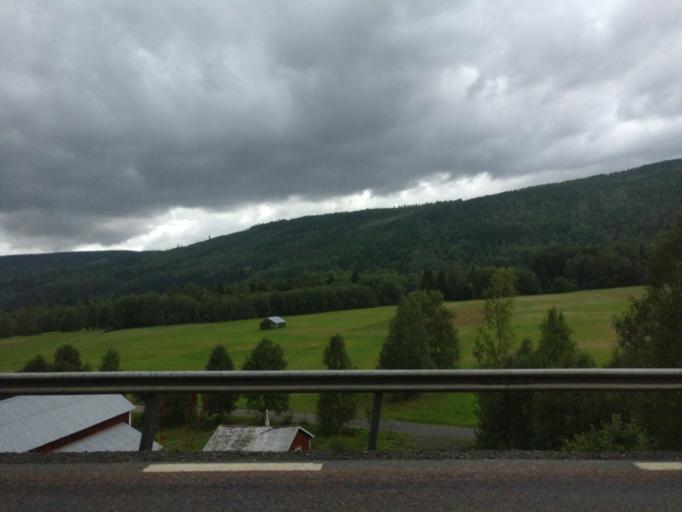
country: SE
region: Vaermland
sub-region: Torsby Kommun
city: Torsby
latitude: 60.7027
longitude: 12.9044
